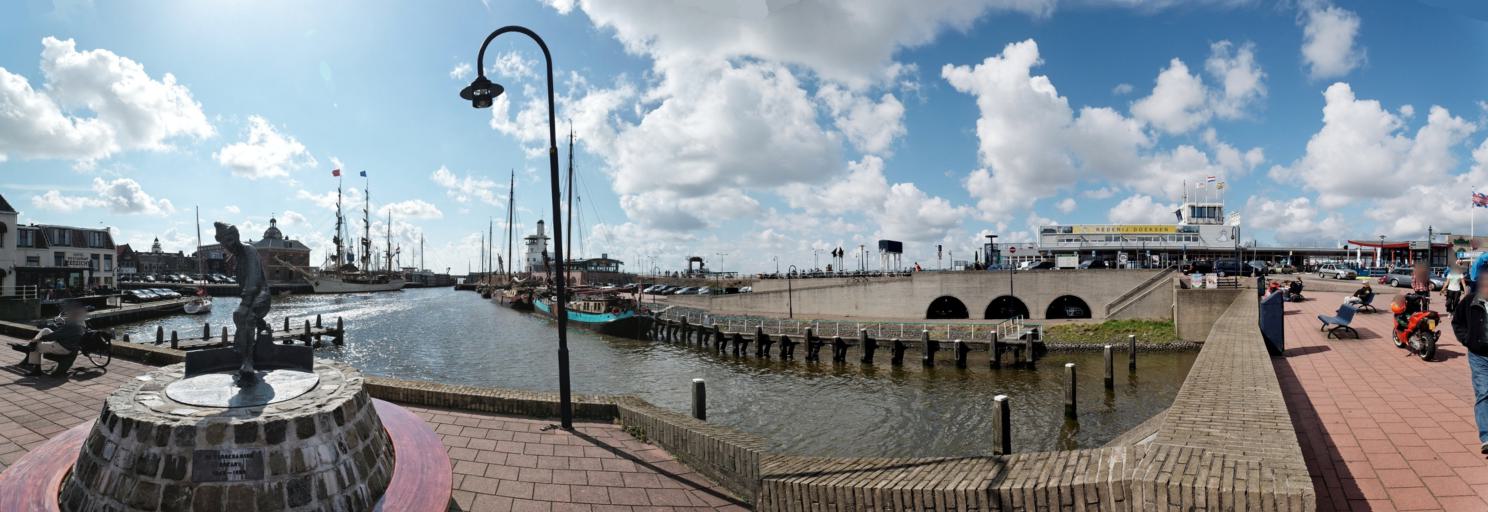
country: NL
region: Friesland
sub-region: Gemeente Harlingen
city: Harlingen
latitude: 53.1759
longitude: 5.4139
